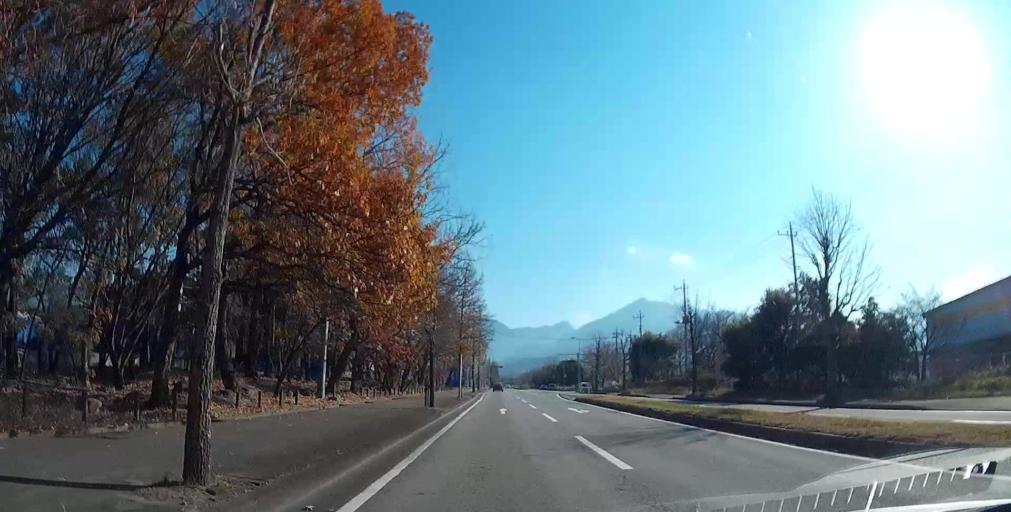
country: JP
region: Yamanashi
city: Isawa
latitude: 35.6279
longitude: 138.6837
